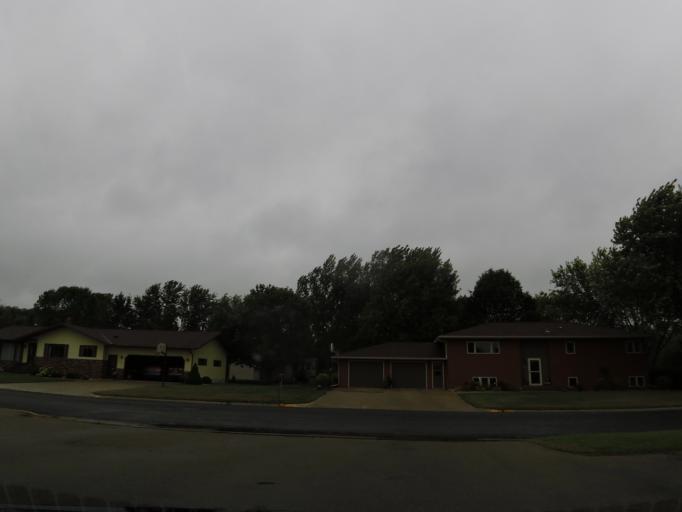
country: US
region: Minnesota
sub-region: Marshall County
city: Warren
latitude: 48.1911
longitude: -96.7755
